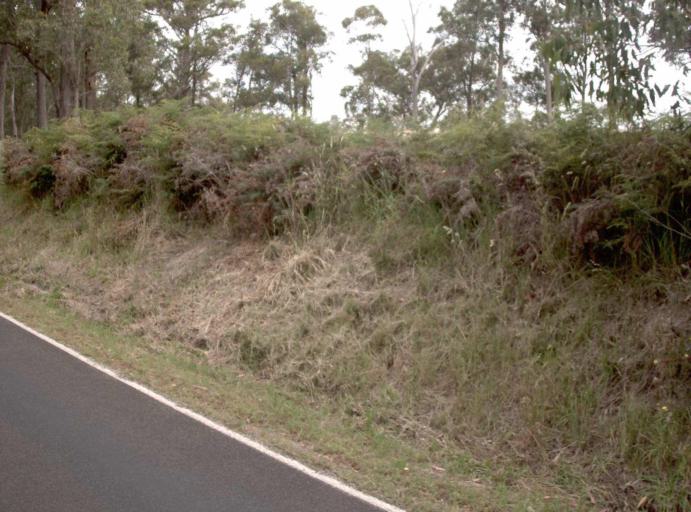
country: AU
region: Victoria
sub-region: Latrobe
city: Traralgon
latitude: -38.3839
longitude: 146.7978
